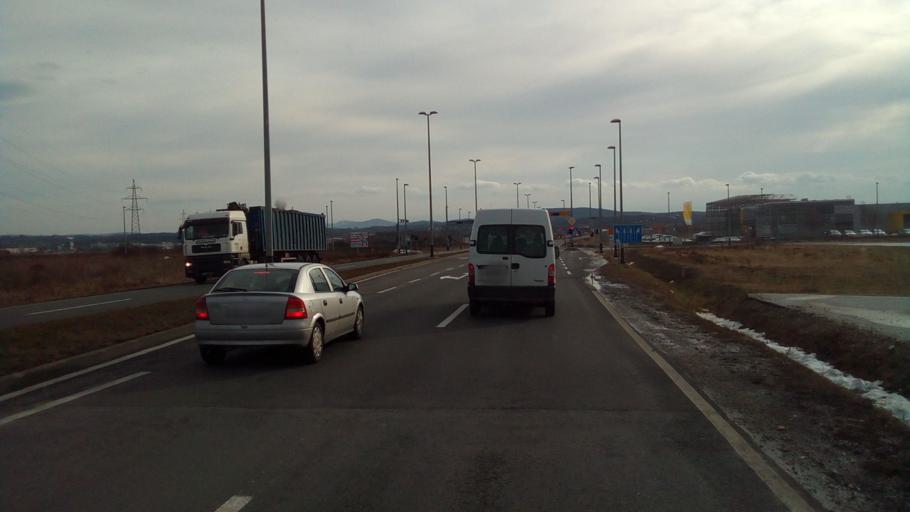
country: HR
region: Varazdinska
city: Varazdin
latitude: 46.2744
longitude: 16.3607
